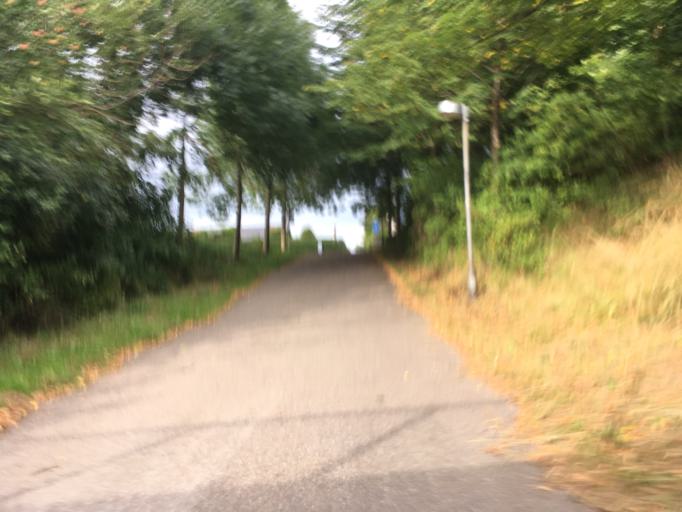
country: DK
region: Capital Region
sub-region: Hillerod Kommune
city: Hillerod
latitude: 55.9341
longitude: 12.2760
